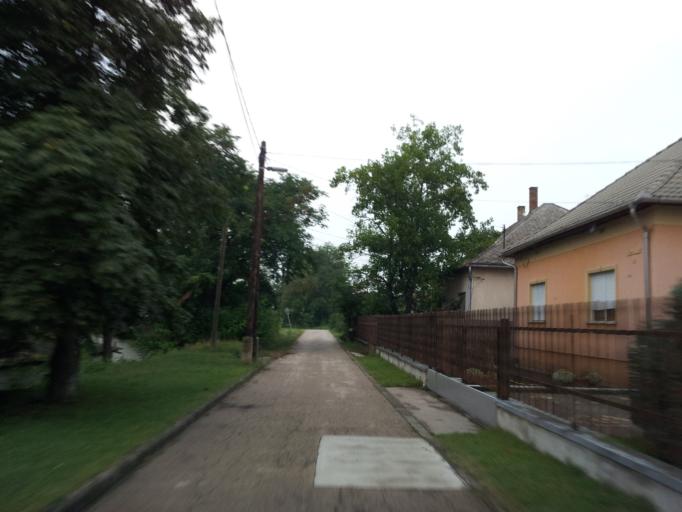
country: HU
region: Tolna
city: Tolna
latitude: 46.4224
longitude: 18.7713
